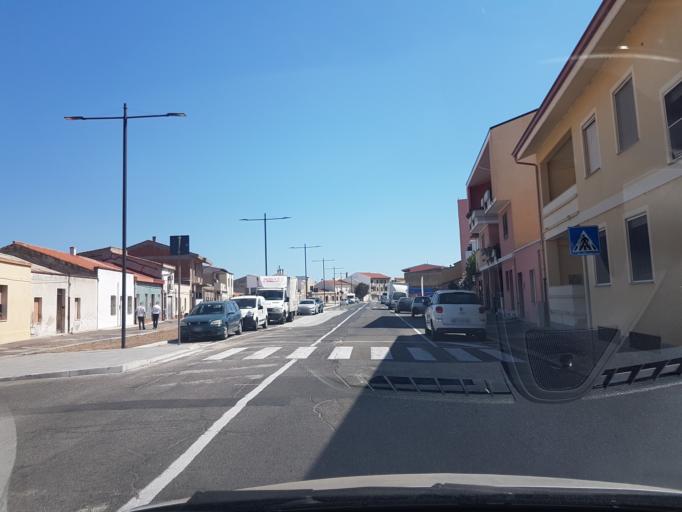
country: IT
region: Sardinia
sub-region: Provincia di Oristano
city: Oristano
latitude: 39.8995
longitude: 8.5958
